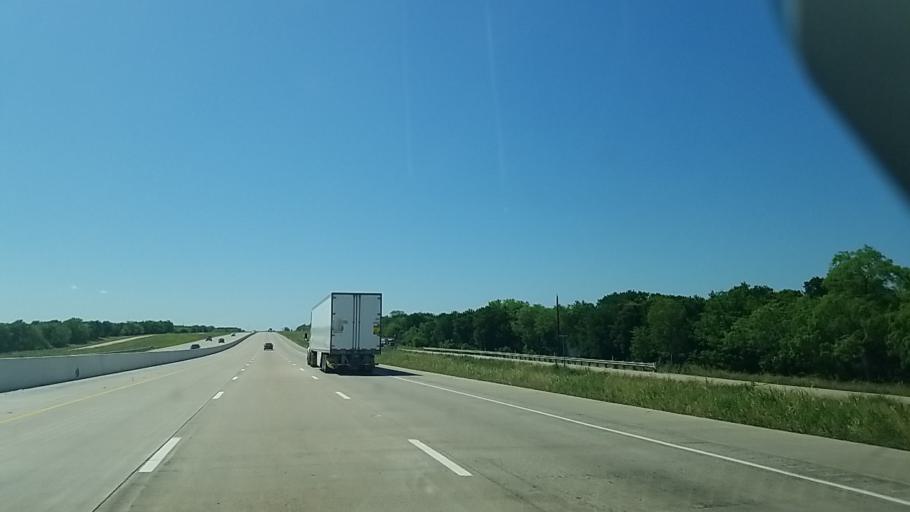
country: US
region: Texas
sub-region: Freestone County
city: Wortham
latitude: 31.8948
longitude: -96.3648
